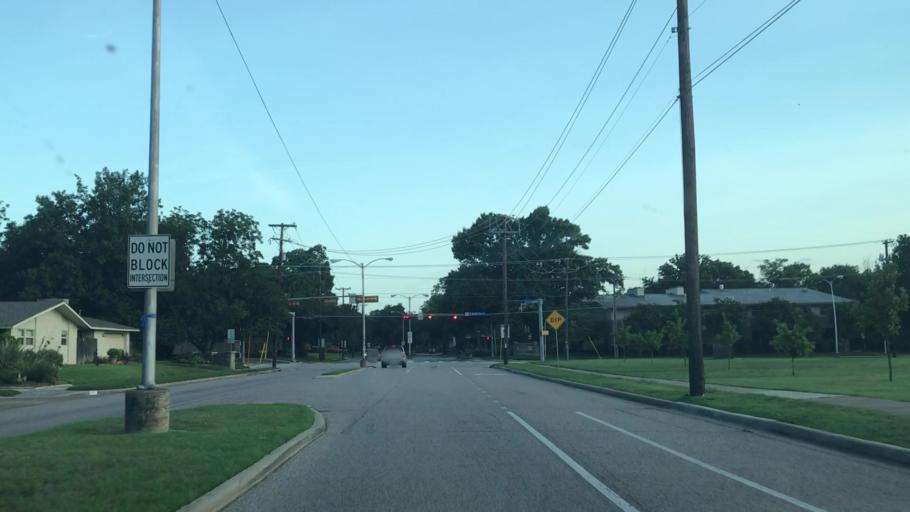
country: US
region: Texas
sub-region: Dallas County
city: Richardson
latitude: 32.9632
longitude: -96.7559
